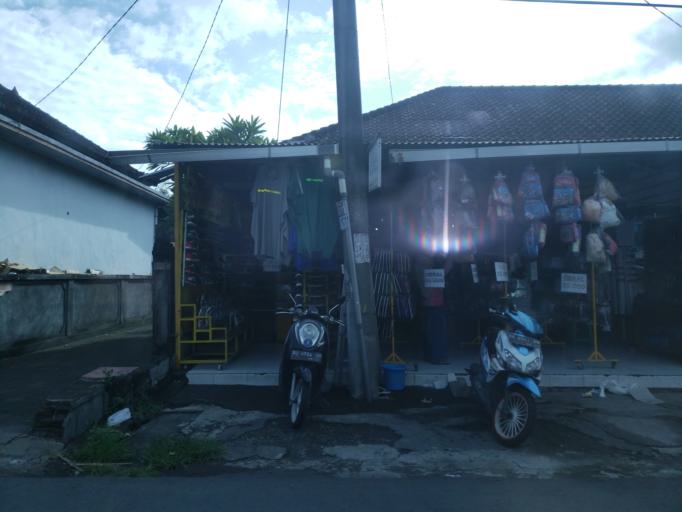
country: ID
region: Bali
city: Karyadharma
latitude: -8.6784
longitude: 115.1807
